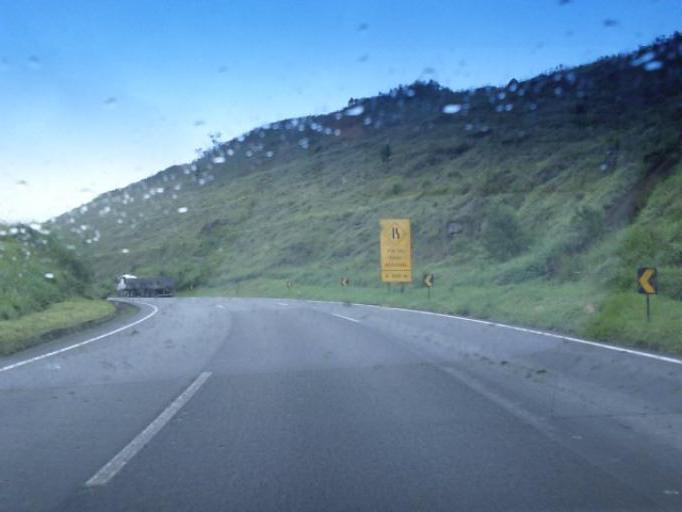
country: BR
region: Sao Paulo
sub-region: Cajati
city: Cajati
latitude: -24.9683
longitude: -48.4553
